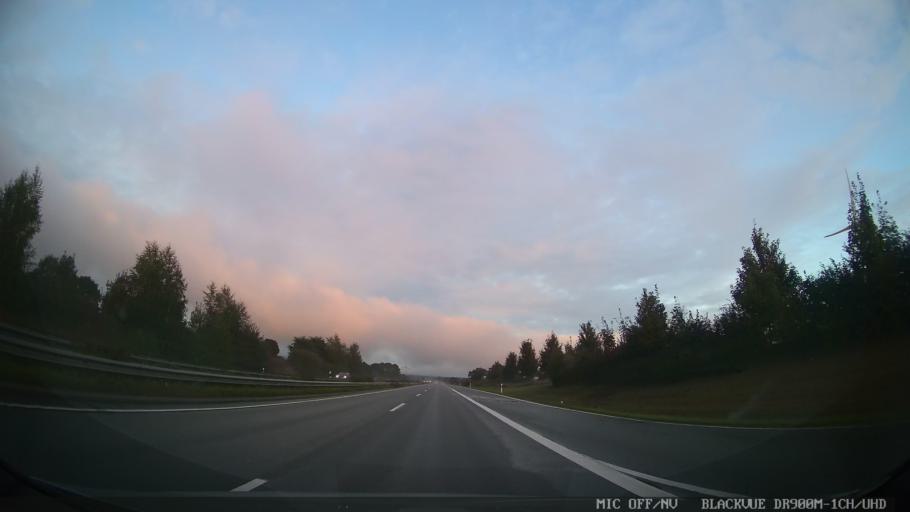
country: DE
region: Schleswig-Holstein
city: Weede
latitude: 53.9180
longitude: 10.3874
